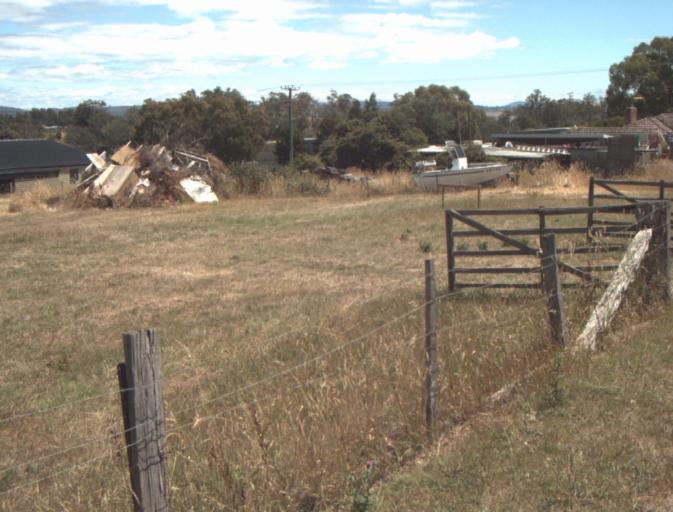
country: AU
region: Tasmania
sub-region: Launceston
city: Mayfield
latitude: -41.3706
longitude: 147.1409
